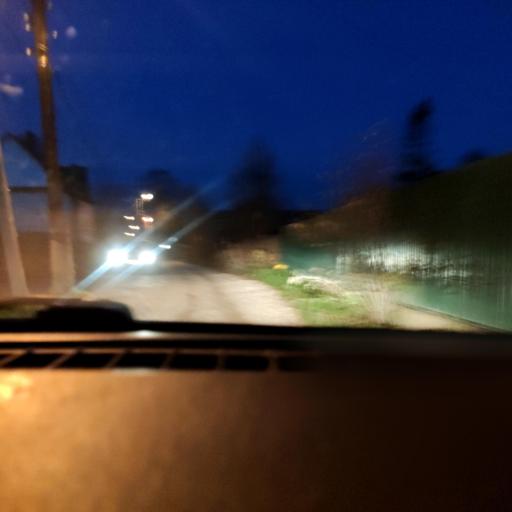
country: RU
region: Perm
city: Perm
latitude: 58.0499
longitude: 56.3332
